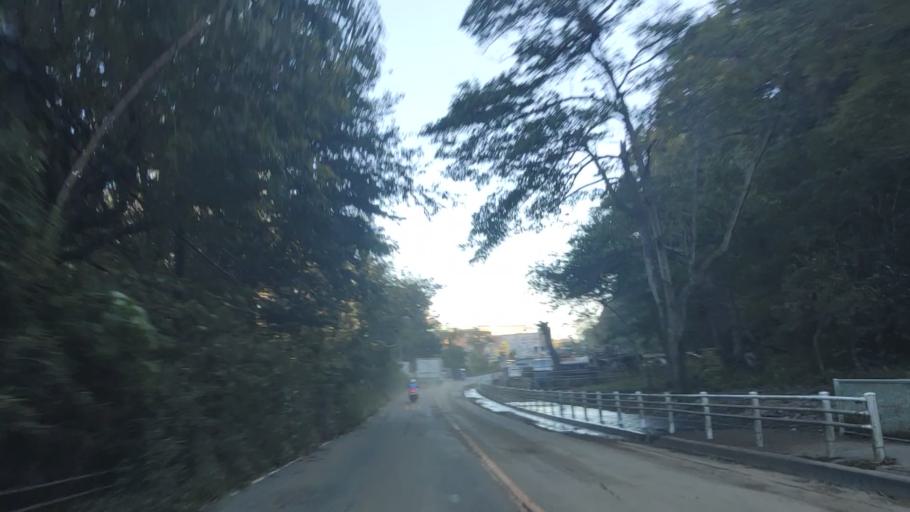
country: JP
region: Tokyo
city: Hachioji
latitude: 35.5744
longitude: 139.3052
